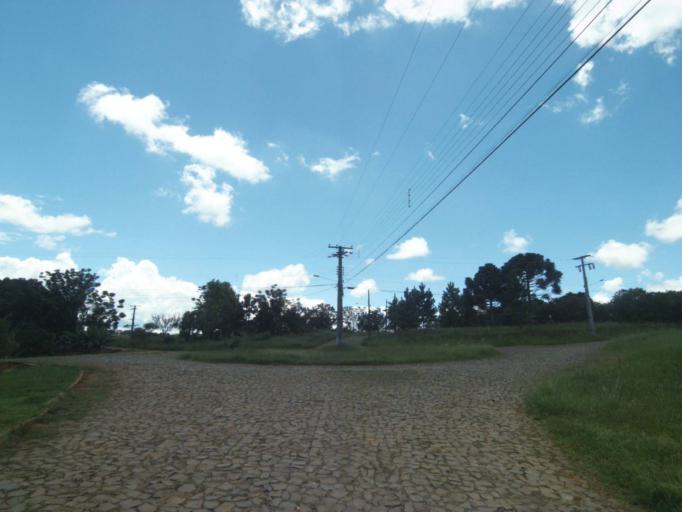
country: BR
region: Parana
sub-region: Pinhao
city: Pinhao
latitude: -25.7907
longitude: -52.0826
